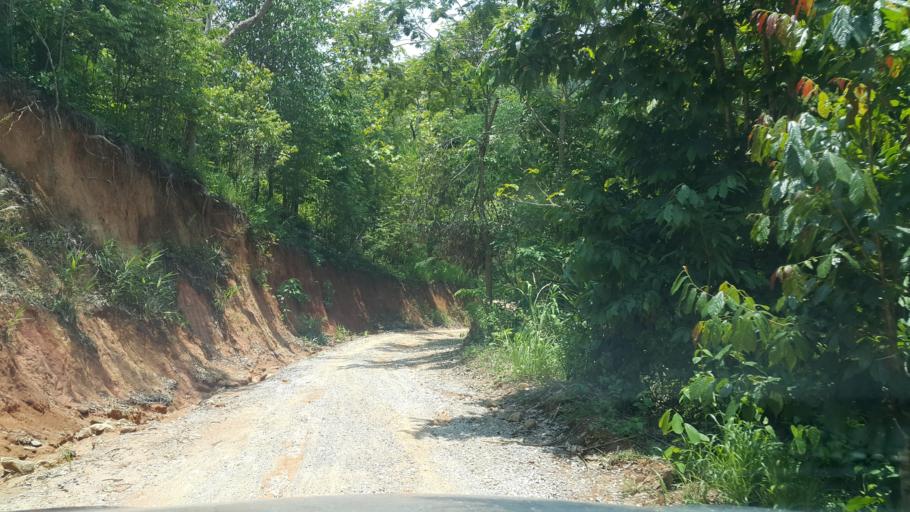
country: TH
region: Chiang Rai
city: Chiang Rai
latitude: 20.0011
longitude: 99.7195
